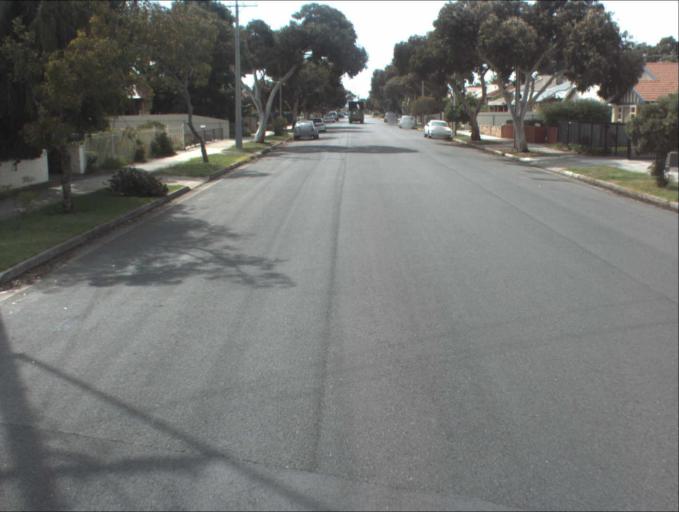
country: AU
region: South Australia
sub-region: Port Adelaide Enfield
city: Birkenhead
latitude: -34.8258
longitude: 138.4960
